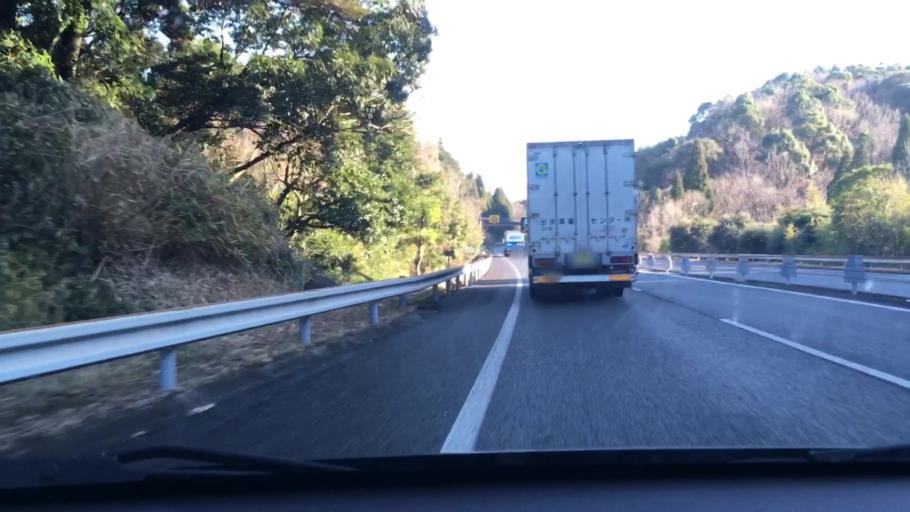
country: JP
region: Kagoshima
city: Kajiki
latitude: 31.8341
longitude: 130.6909
